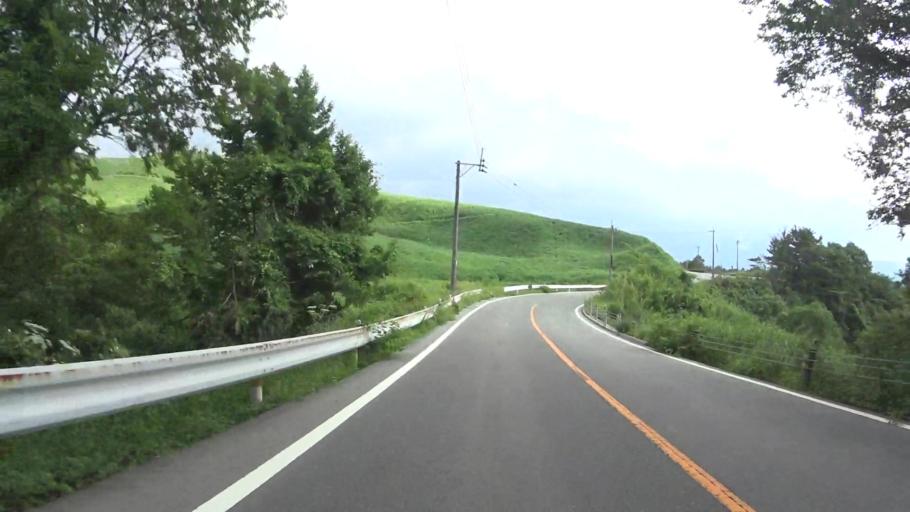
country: JP
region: Kumamoto
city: Aso
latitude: 32.8973
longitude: 131.0282
